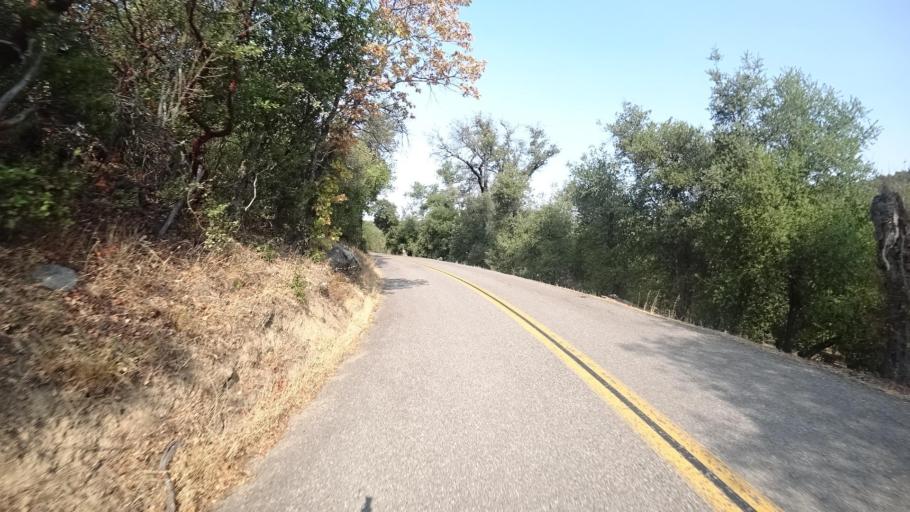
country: US
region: California
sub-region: San Diego County
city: Julian
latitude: 33.0949
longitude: -116.6322
